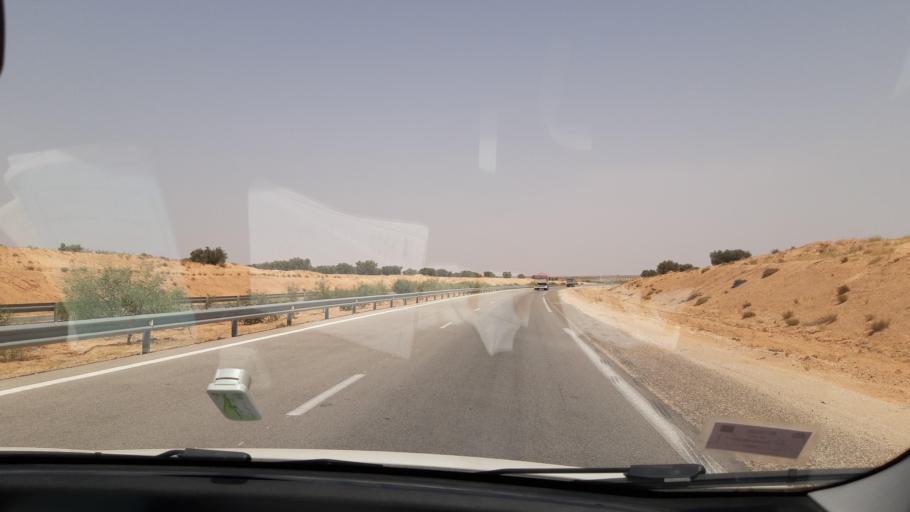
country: TN
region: Safaqis
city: Bi'r `Ali Bin Khalifah
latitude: 34.5274
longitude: 10.0850
